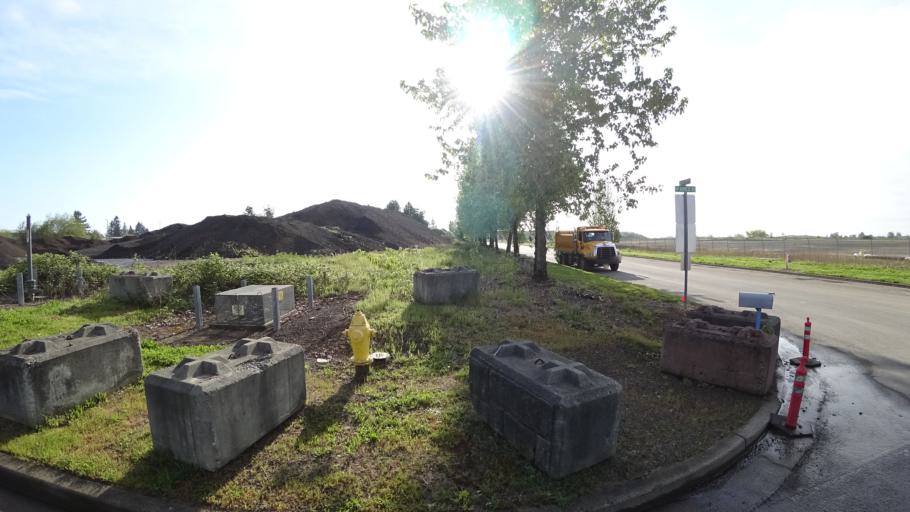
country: US
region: Oregon
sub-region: Washington County
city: Hillsboro
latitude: 45.5127
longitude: -123.0013
